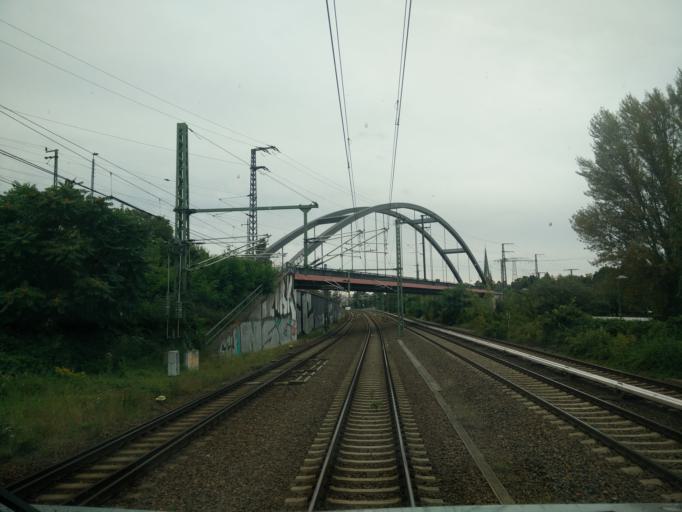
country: DE
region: Berlin
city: Rummelsburg
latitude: 52.4983
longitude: 13.4864
